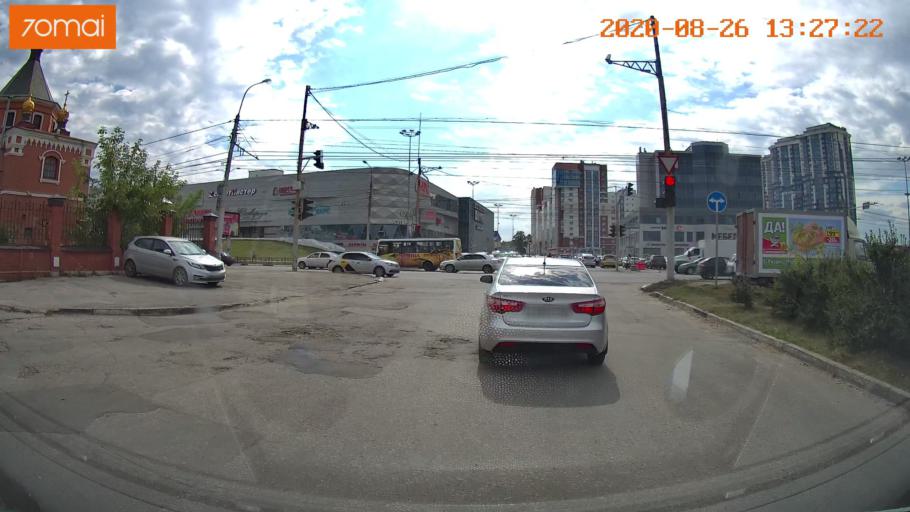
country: RU
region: Rjazan
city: Ryazan'
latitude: 54.6336
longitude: 39.6981
